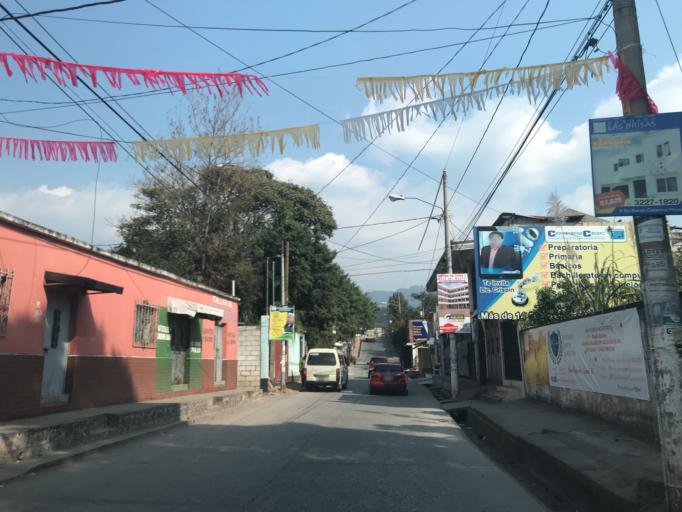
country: GT
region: Guatemala
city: Santa Catarina Pinula
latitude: 14.5499
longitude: -90.5246
